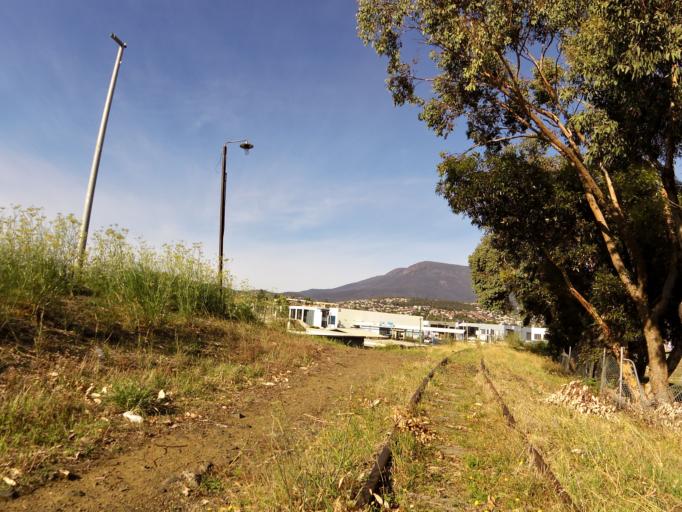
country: AU
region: Tasmania
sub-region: Glenorchy
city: Lutana
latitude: -42.8364
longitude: 147.3036
